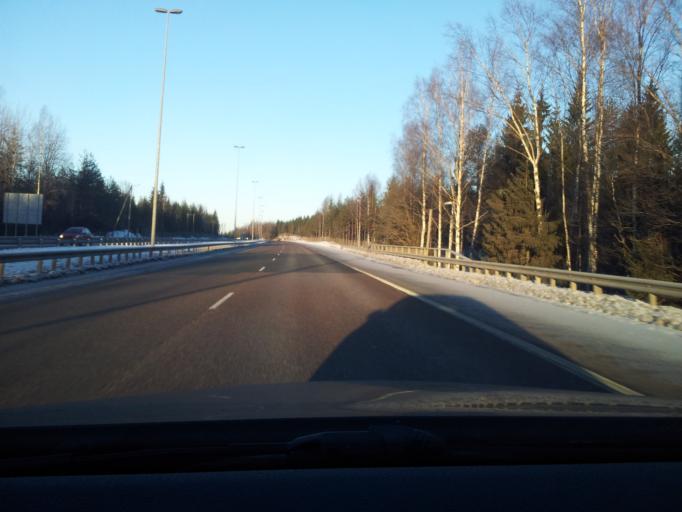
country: FI
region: Uusimaa
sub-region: Helsinki
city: Espoo
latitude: 60.2535
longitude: 24.5245
